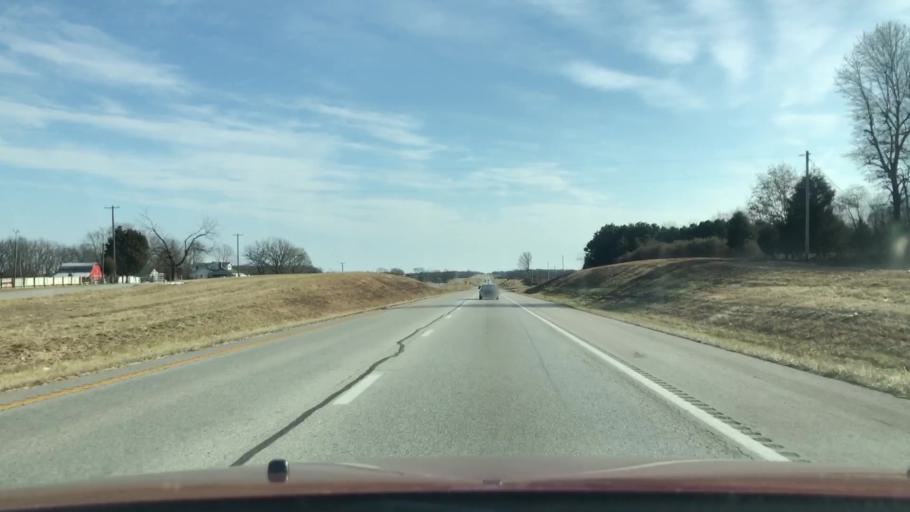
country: US
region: Missouri
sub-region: Webster County
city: Rogersville
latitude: 37.1194
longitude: -93.1610
